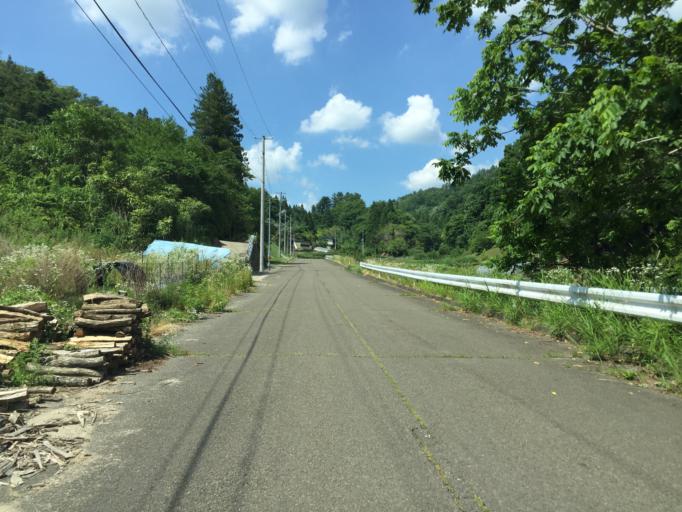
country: JP
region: Fukushima
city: Yanagawamachi-saiwaicho
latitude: 37.7680
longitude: 140.6519
